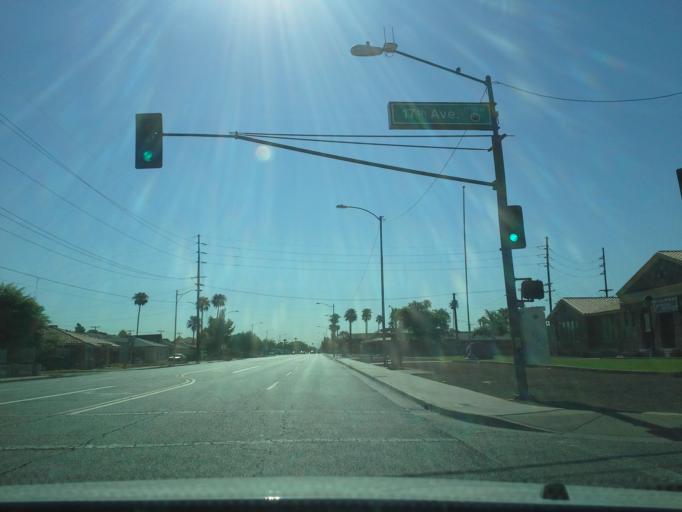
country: US
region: Arizona
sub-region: Maricopa County
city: Phoenix
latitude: 33.4658
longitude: -112.0956
